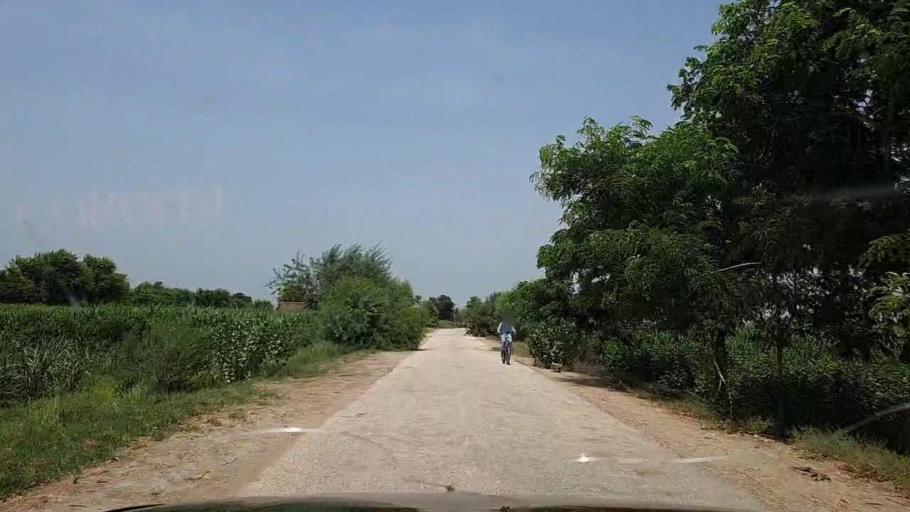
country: PK
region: Sindh
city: Ghotki
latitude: 28.0169
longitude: 69.3546
